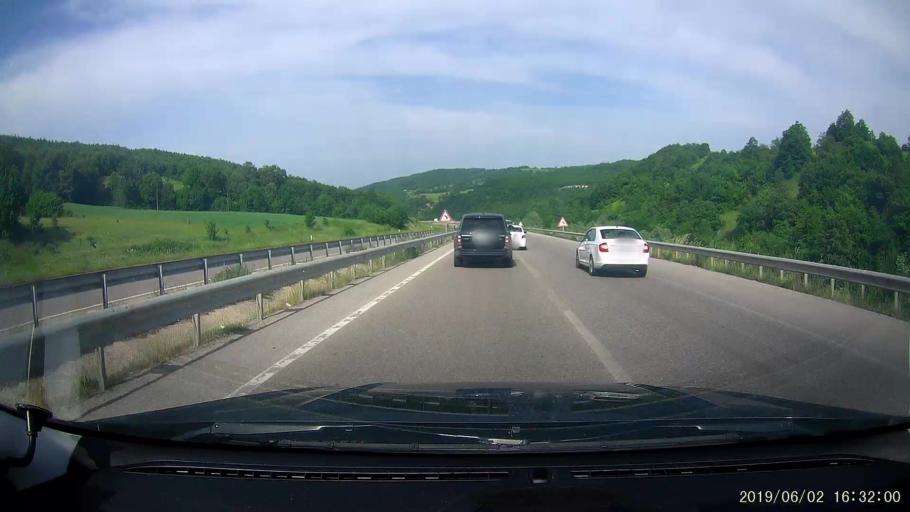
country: TR
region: Samsun
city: Ladik
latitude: 41.0363
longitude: 35.9109
